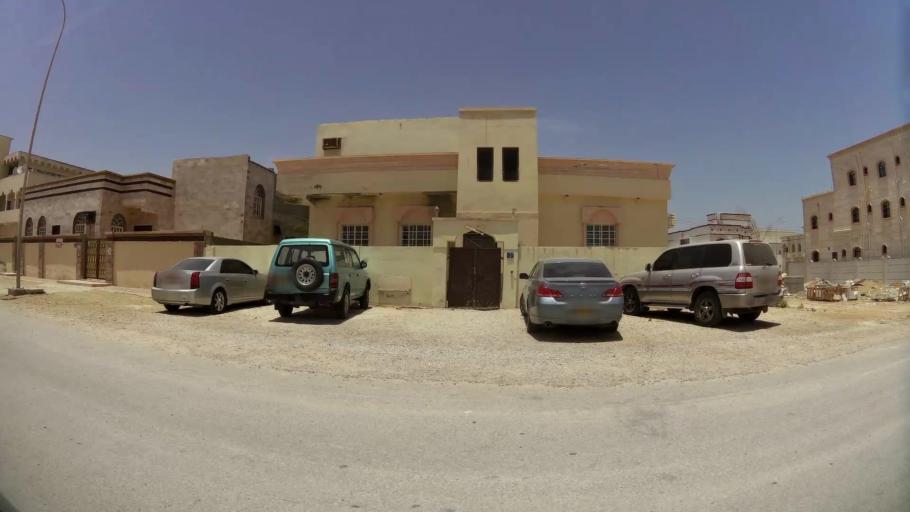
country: OM
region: Zufar
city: Salalah
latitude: 17.0746
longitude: 54.1586
